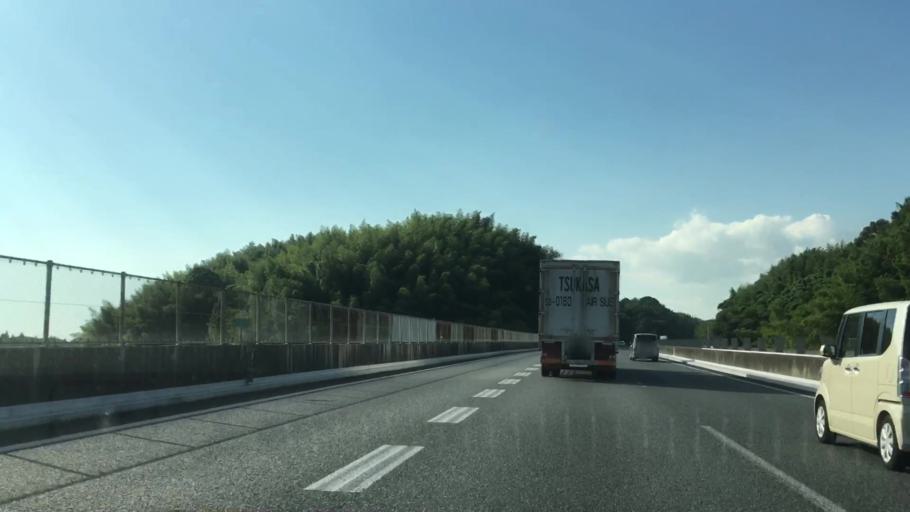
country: JP
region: Yamaguchi
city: Kudamatsu
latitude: 34.0316
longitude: 131.9352
